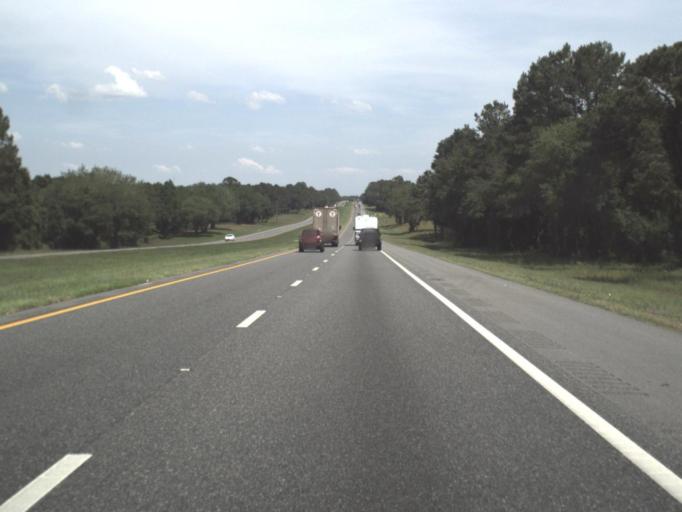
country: US
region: Florida
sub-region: Columbia County
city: Five Points
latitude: 30.2550
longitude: -82.7182
